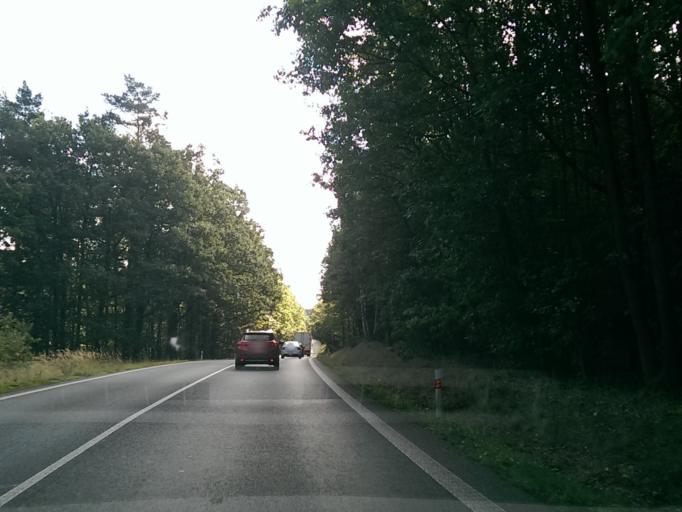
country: CZ
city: Doksy
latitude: 50.5949
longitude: 14.6100
